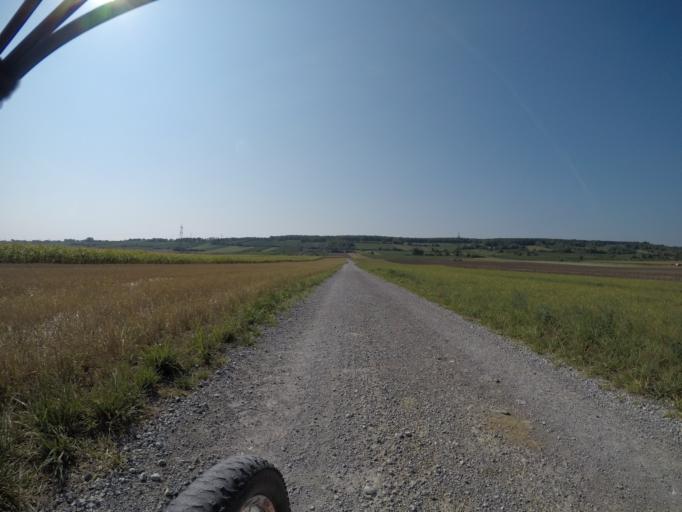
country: AT
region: Lower Austria
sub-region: Politischer Bezirk Baden
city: Hirtenberg
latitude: 47.9522
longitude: 16.1872
